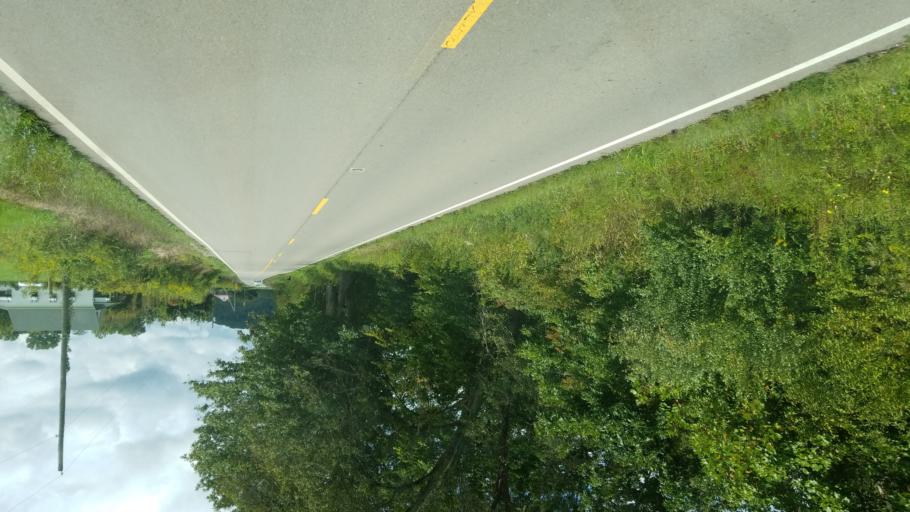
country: US
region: Ohio
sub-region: Scioto County
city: Sciotodale
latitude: 38.8877
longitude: -82.7559
